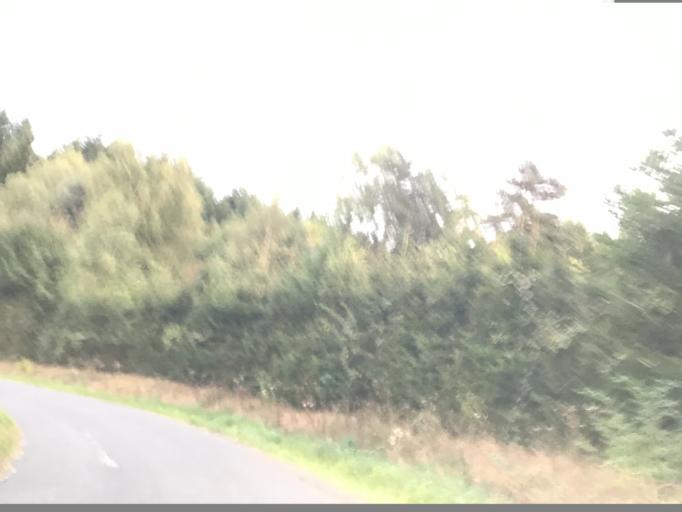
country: FR
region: Auvergne
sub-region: Departement du Puy-de-Dome
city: La Monnerie-le-Montel
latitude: 45.8410
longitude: 3.6118
